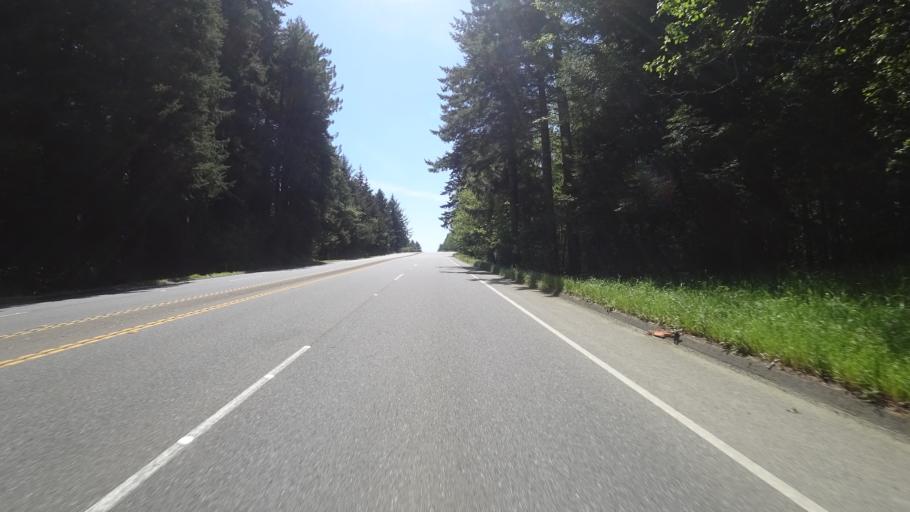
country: US
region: California
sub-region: Humboldt County
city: Westhaven-Moonstone
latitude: 41.0412
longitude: -124.1149
